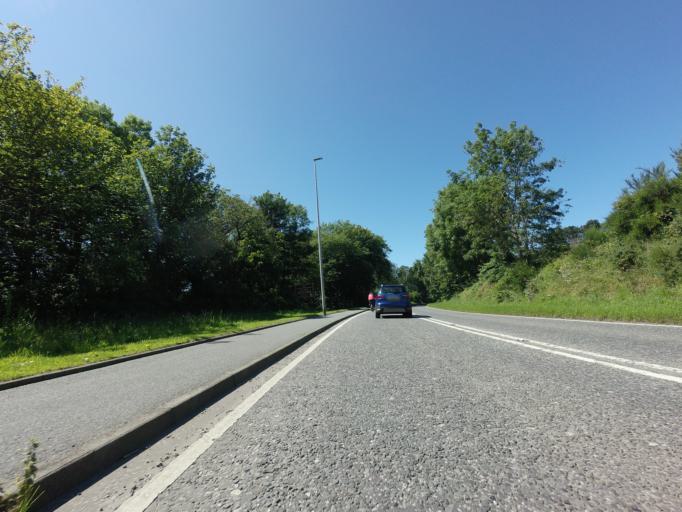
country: GB
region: Scotland
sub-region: Aberdeenshire
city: Macduff
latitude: 57.6587
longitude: -2.5081
